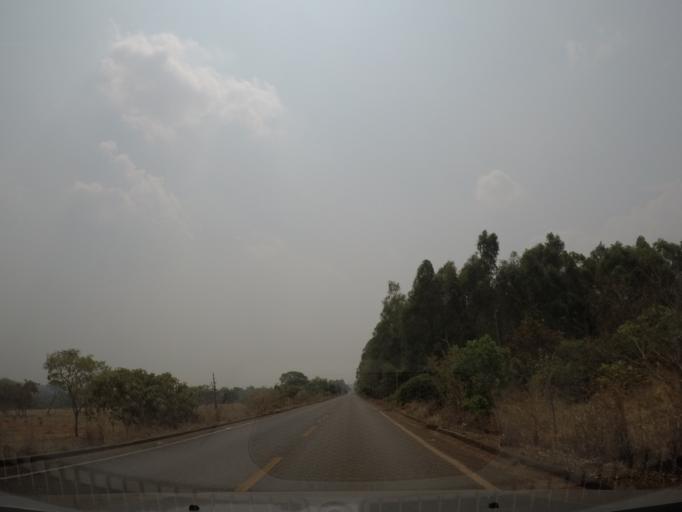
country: BR
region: Goias
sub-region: Pirenopolis
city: Pirenopolis
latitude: -15.9146
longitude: -48.8587
